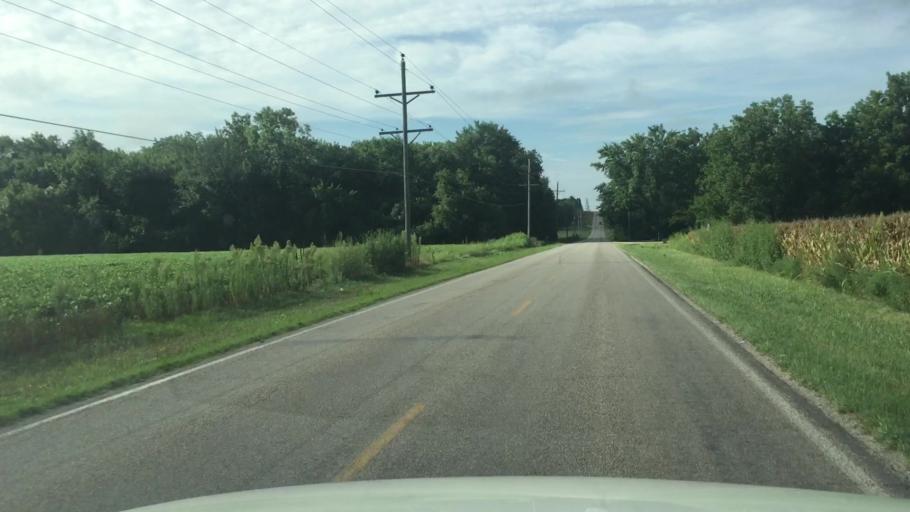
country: US
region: Kansas
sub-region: Allen County
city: Humboldt
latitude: 37.8686
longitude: -95.4369
